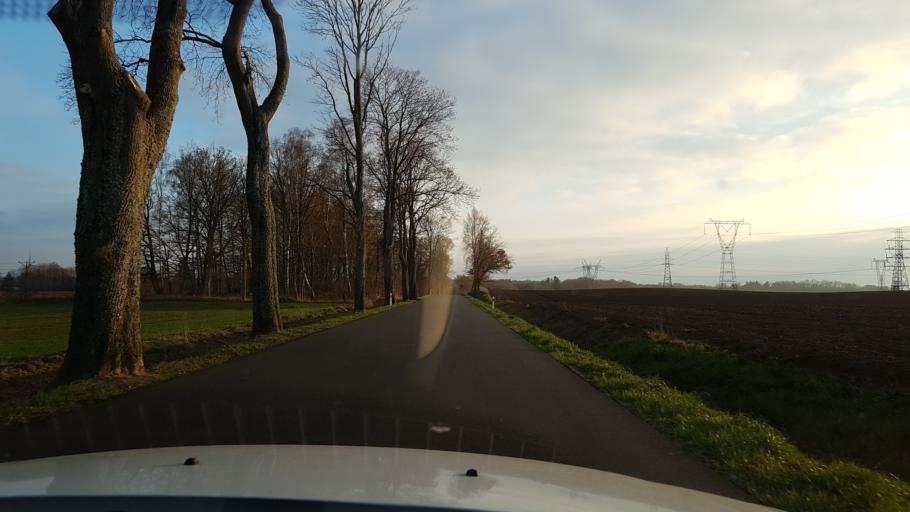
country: PL
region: West Pomeranian Voivodeship
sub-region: Koszalin
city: Koszalin
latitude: 54.1309
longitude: 16.0870
